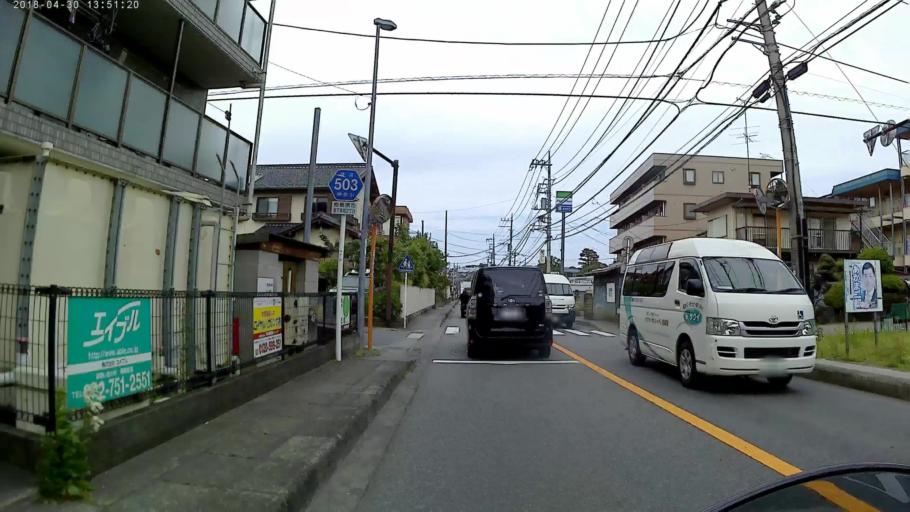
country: JP
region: Tokyo
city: Hachioji
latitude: 35.5914
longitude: 139.3728
